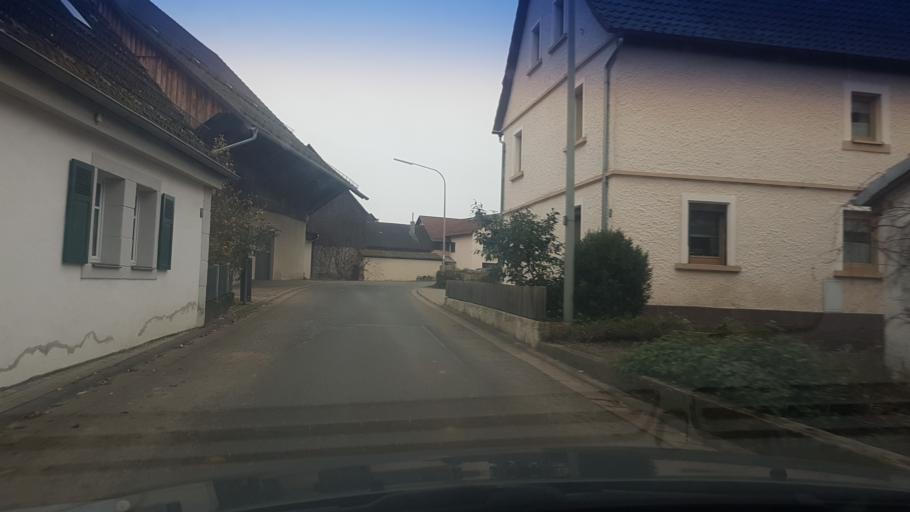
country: DE
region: Bavaria
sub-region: Upper Franconia
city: Wonsees
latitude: 50.0341
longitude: 11.2932
